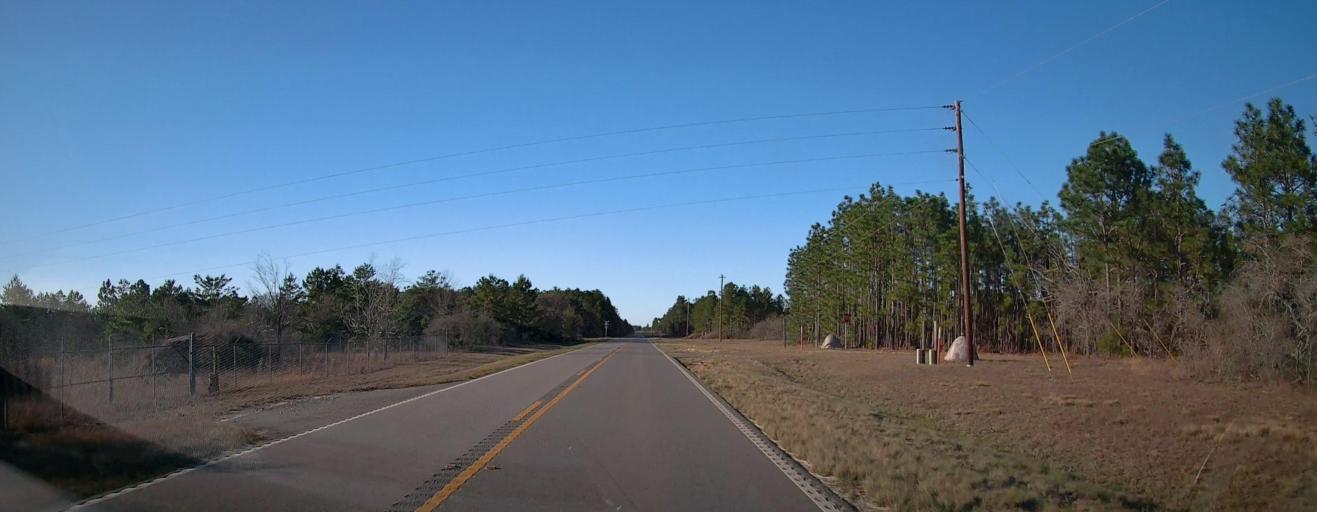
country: US
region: Georgia
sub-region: Talbot County
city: Talbotton
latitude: 32.5718
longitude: -84.4417
